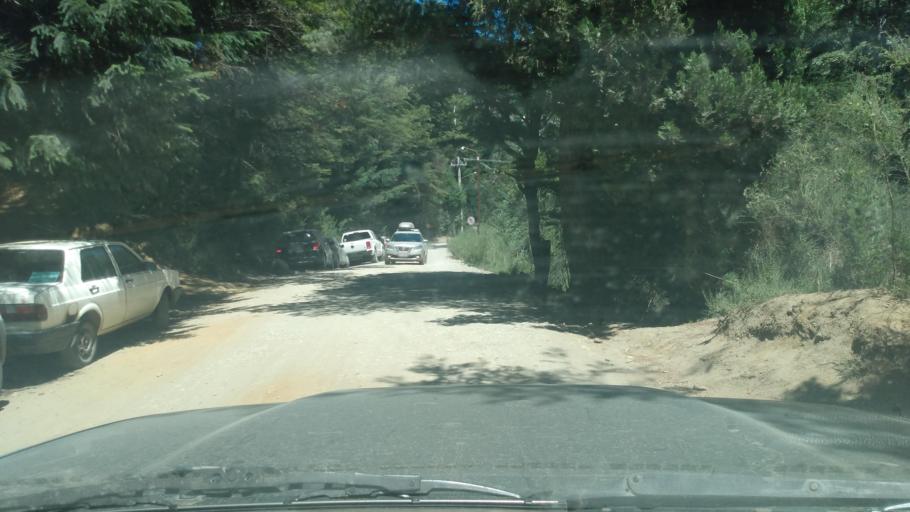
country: AR
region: Rio Negro
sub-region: Departamento de Bariloche
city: San Carlos de Bariloche
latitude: -41.0966
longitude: -71.5177
